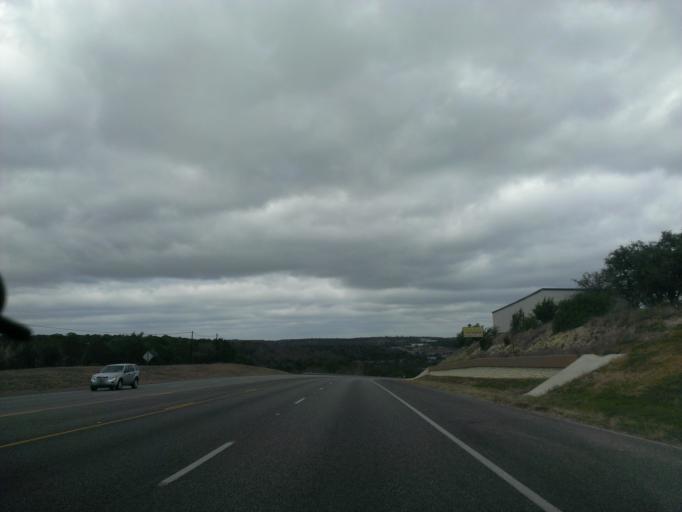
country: US
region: Texas
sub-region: Travis County
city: The Hills
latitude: 30.3327
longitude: -98.0262
